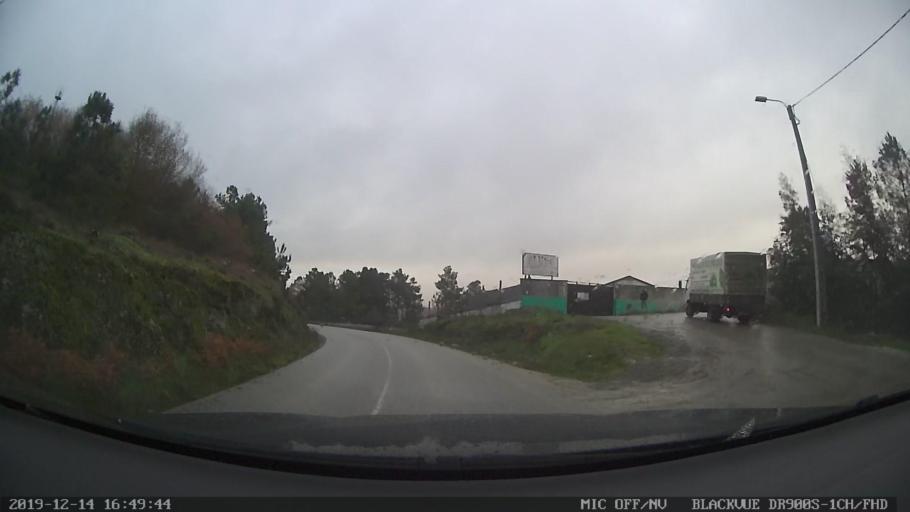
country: PT
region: Vila Real
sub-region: Murca
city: Murca
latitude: 41.4111
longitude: -7.4998
